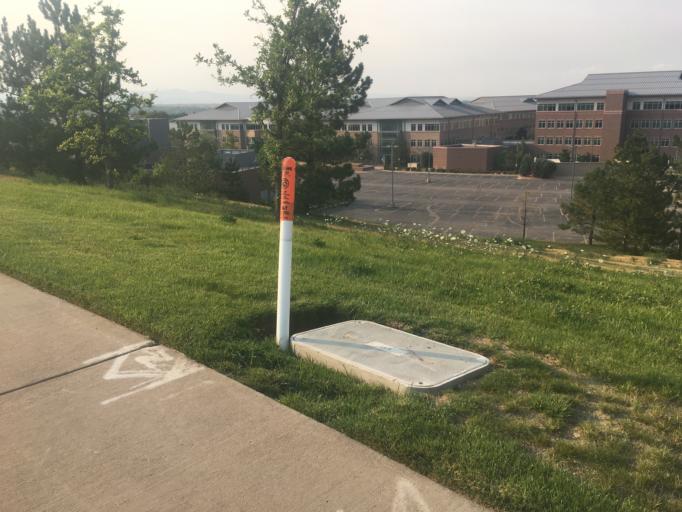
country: US
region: Colorado
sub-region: Broomfield County
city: Broomfield
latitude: 39.9170
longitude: -105.1250
